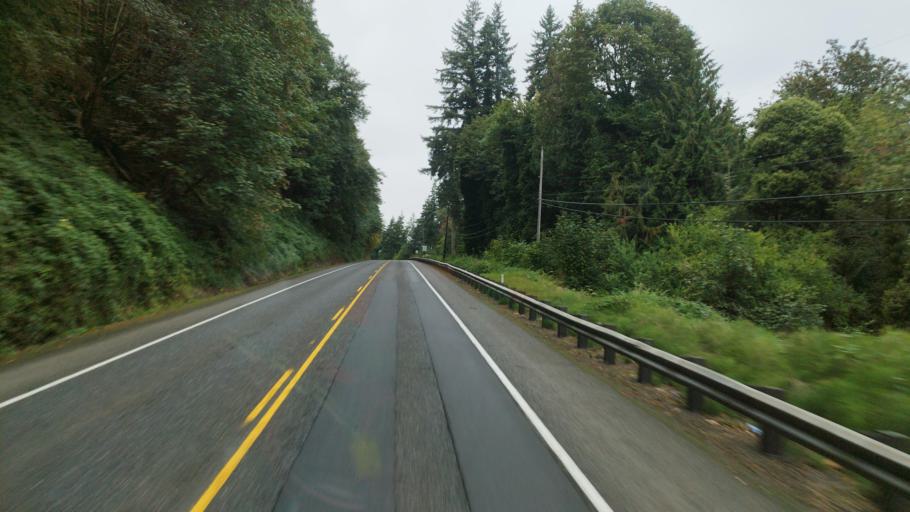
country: US
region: Oregon
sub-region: Columbia County
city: Rainier
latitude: 46.0860
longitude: -122.9227
